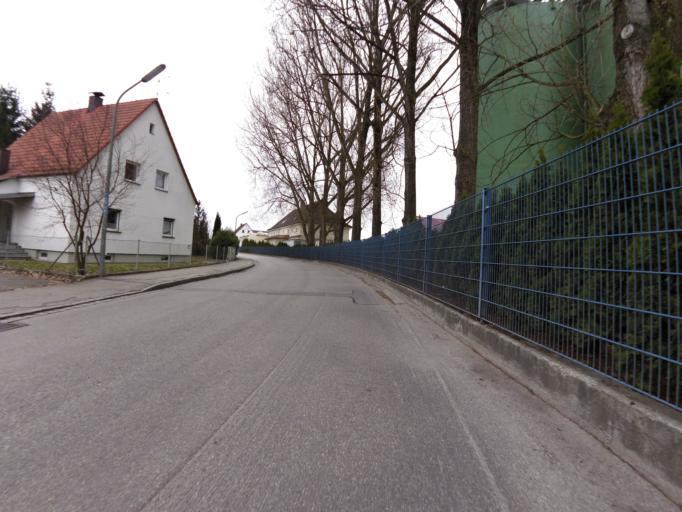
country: DE
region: Bavaria
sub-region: Upper Bavaria
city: Moosburg
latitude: 48.4699
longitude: 11.9437
